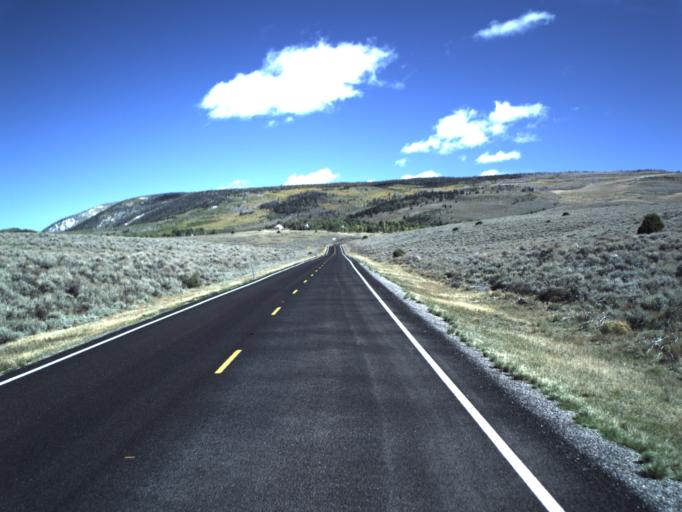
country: US
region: Utah
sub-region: Wayne County
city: Loa
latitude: 38.5040
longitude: -111.7971
